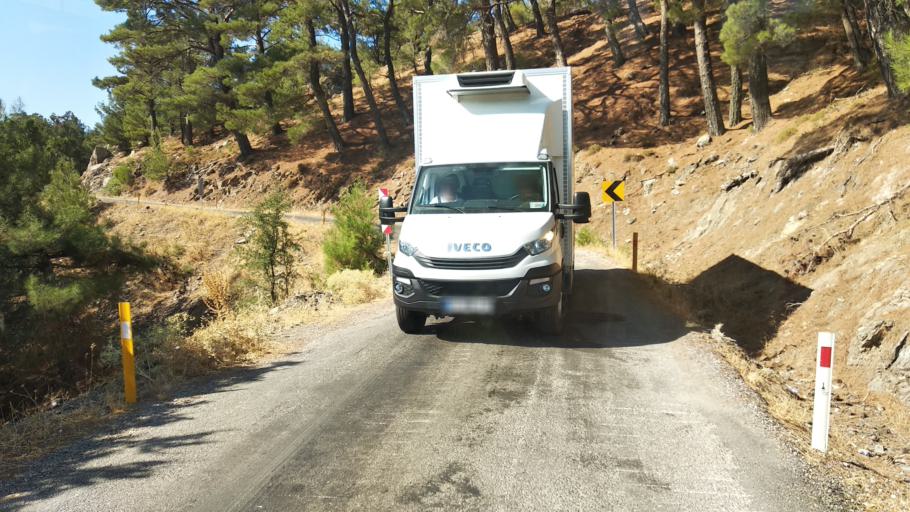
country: TR
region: Izmir
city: Gaziemir
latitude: 38.2971
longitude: 26.9986
